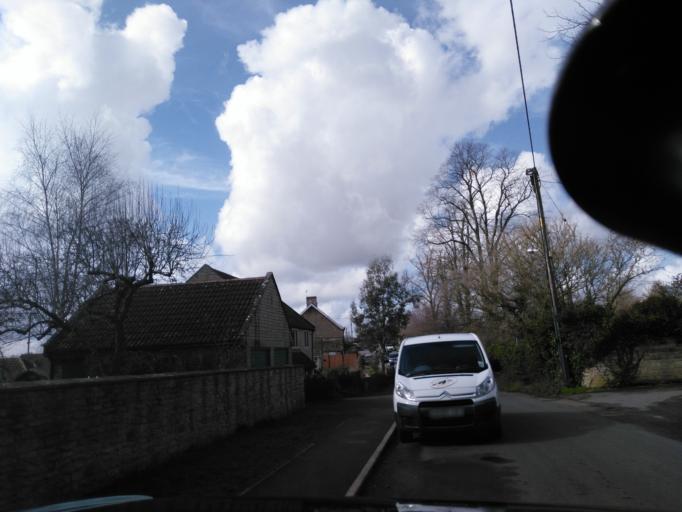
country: GB
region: England
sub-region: Wiltshire
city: Atworth
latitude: 51.3963
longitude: -2.1689
